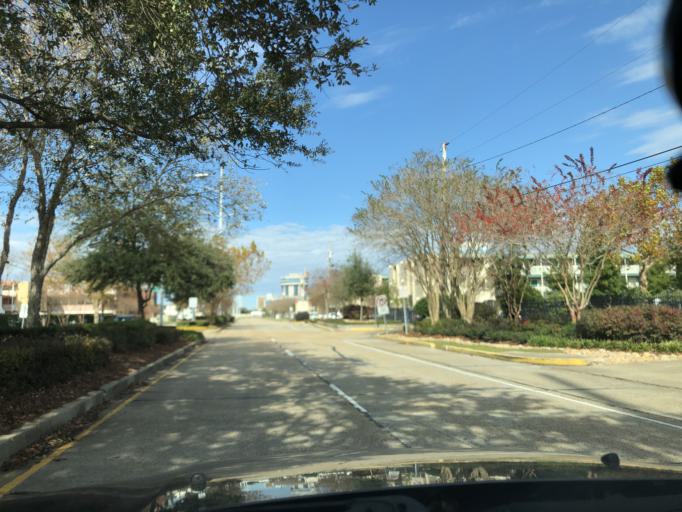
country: US
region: Louisiana
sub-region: Jefferson Parish
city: Metairie
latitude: 29.9937
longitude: -90.1598
